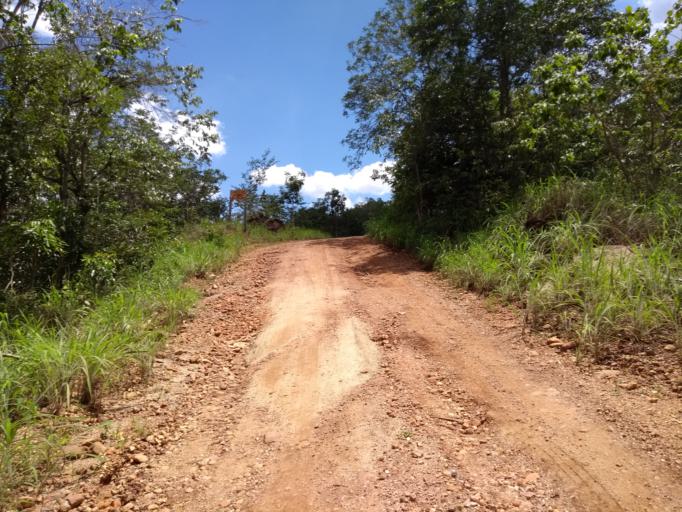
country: BR
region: Goias
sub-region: Pirenopolis
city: Pirenopolis
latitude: -15.6438
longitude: -48.5072
